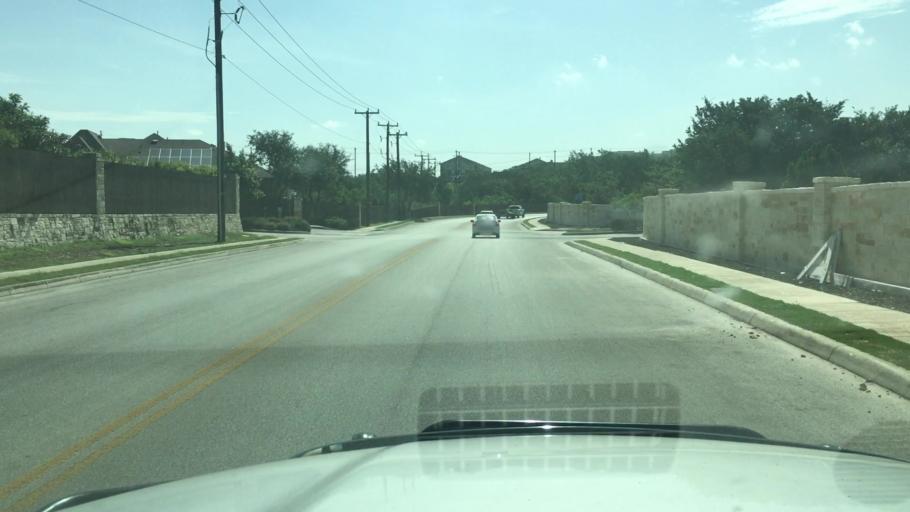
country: US
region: Texas
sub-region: Bexar County
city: Timberwood Park
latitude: 29.6687
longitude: -98.4544
